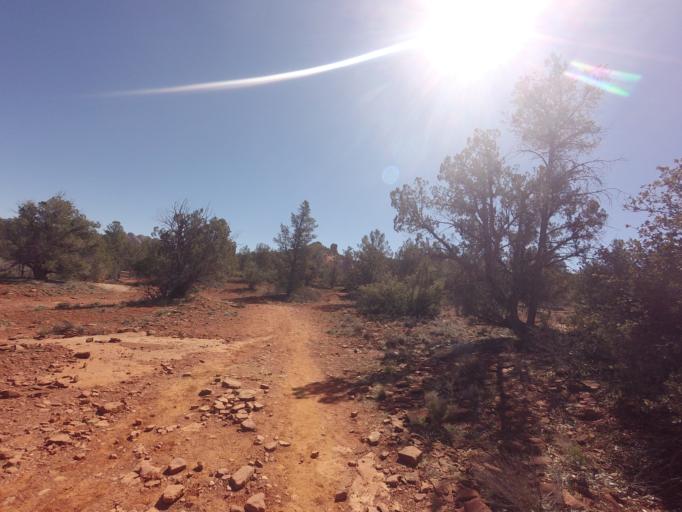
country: US
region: Arizona
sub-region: Yavapai County
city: West Sedona
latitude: 34.8083
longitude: -111.8205
